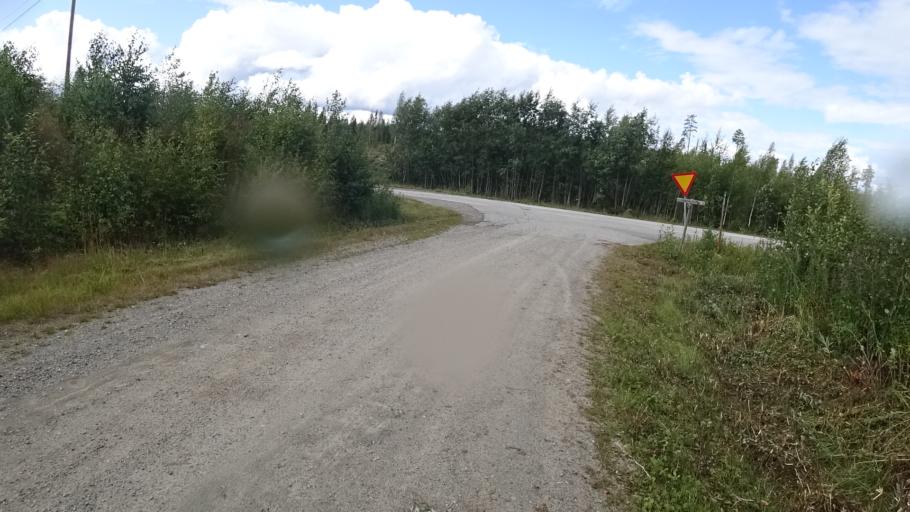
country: FI
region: North Karelia
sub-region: Joensuu
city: Ilomantsi
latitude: 62.6191
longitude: 31.2221
